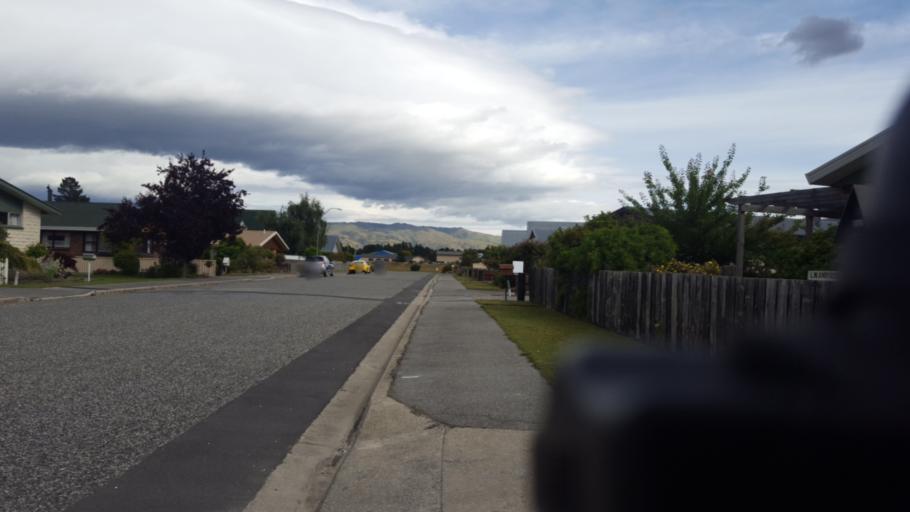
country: NZ
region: Otago
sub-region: Queenstown-Lakes District
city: Wanaka
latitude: -45.2412
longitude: 169.3920
